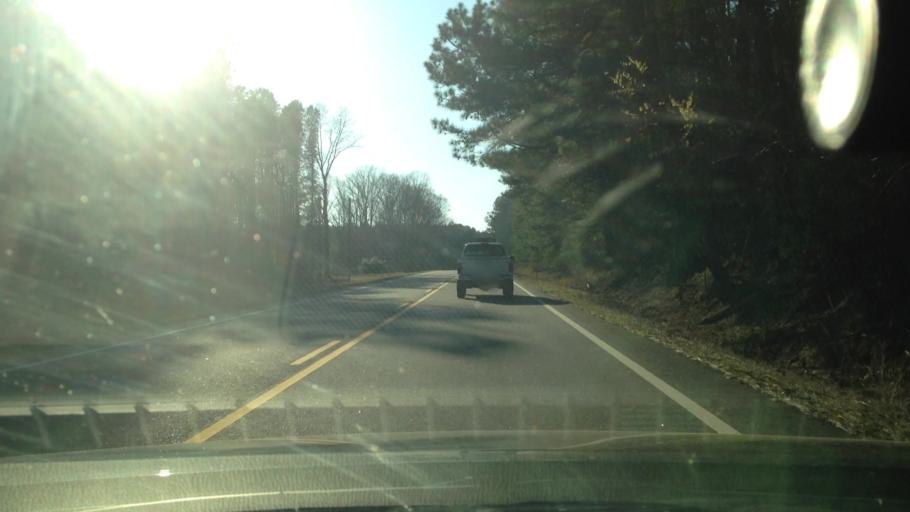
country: US
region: Georgia
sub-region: Fayette County
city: Peachtree City
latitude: 33.3397
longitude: -84.6608
